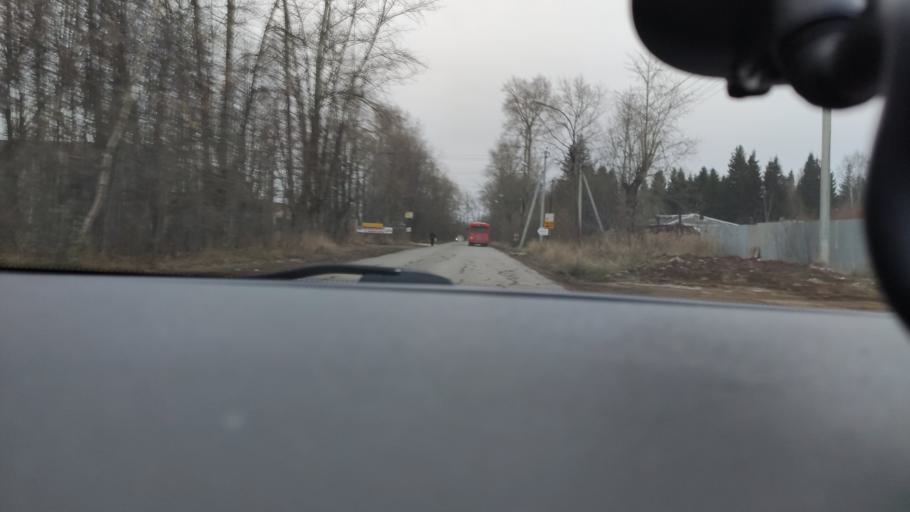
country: RU
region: Perm
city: Perm
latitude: 57.9599
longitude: 56.1963
